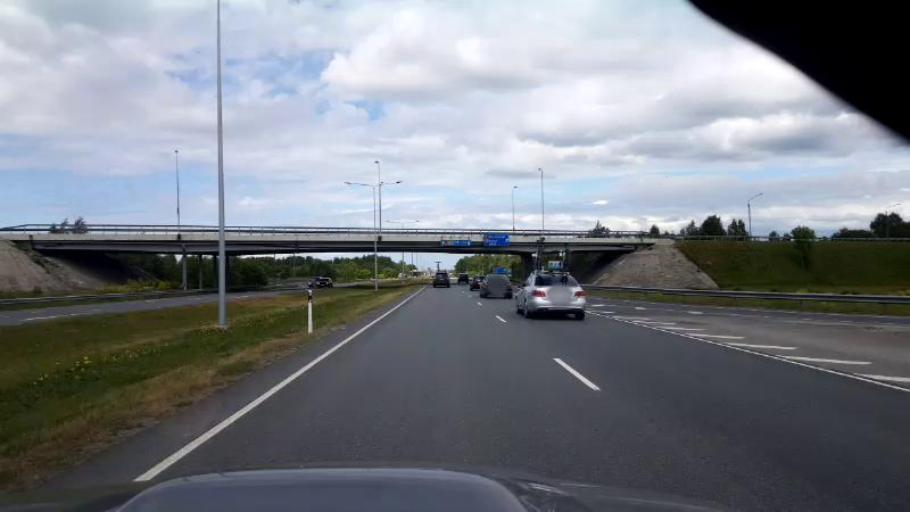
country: EE
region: Harju
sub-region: Saue linn
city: Saue
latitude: 59.3145
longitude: 24.5774
